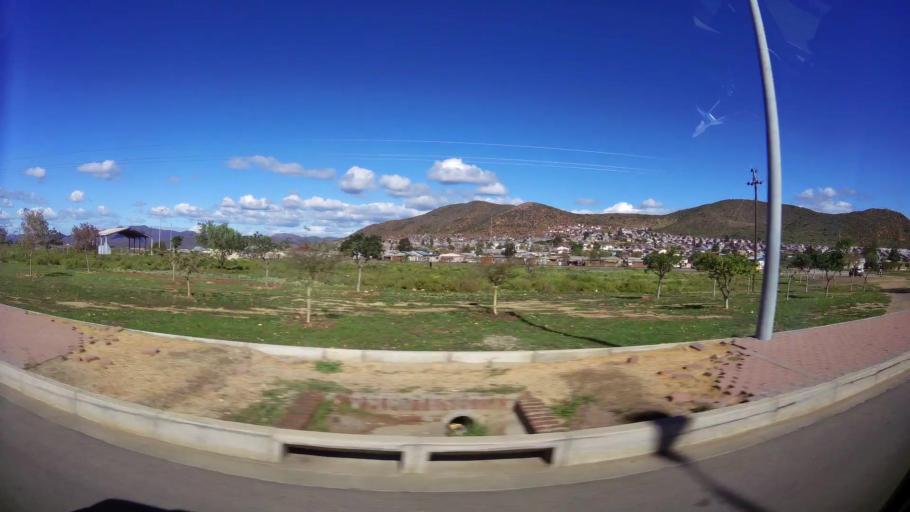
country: ZA
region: Western Cape
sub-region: Cape Winelands District Municipality
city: Ashton
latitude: -33.8150
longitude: 19.8943
